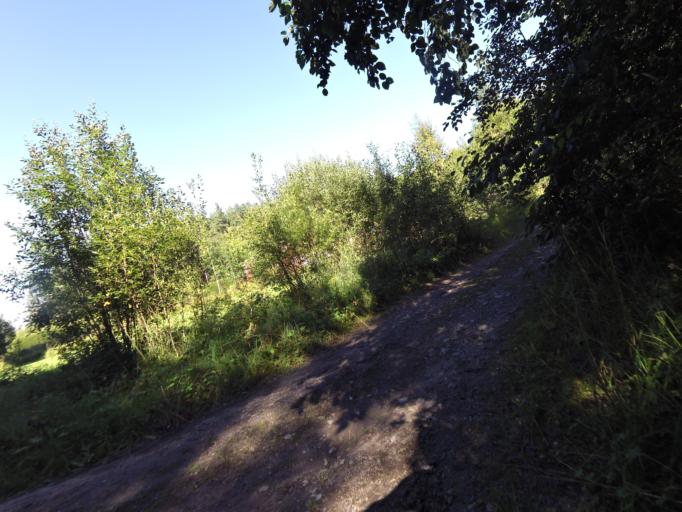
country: SE
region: Gaevleborg
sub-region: Hofors Kommun
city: Hofors
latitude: 60.5462
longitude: 16.3980
